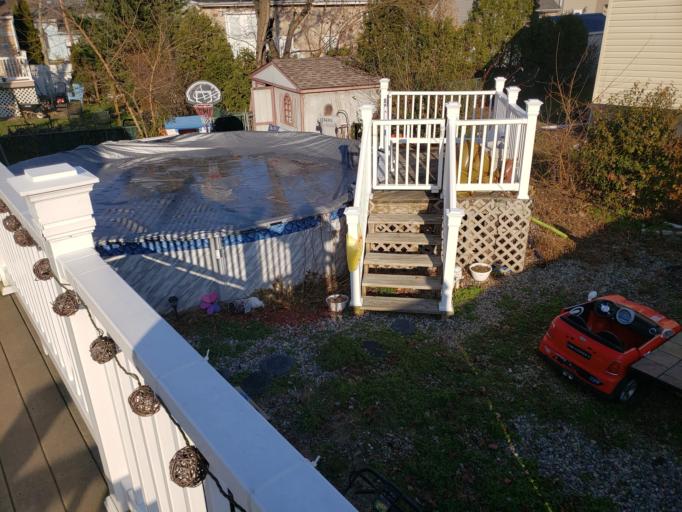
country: US
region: New Jersey
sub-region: Monmouth County
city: Union Beach
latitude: 40.4280
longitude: -74.1692
